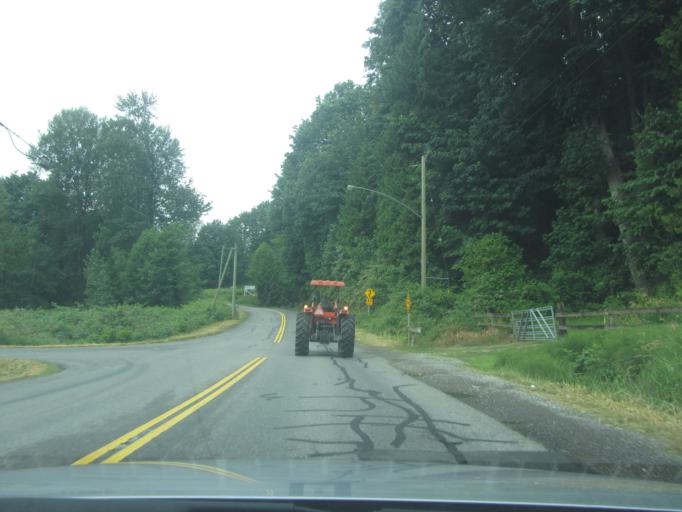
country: CA
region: British Columbia
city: Abbotsford
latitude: 49.1027
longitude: -122.3544
